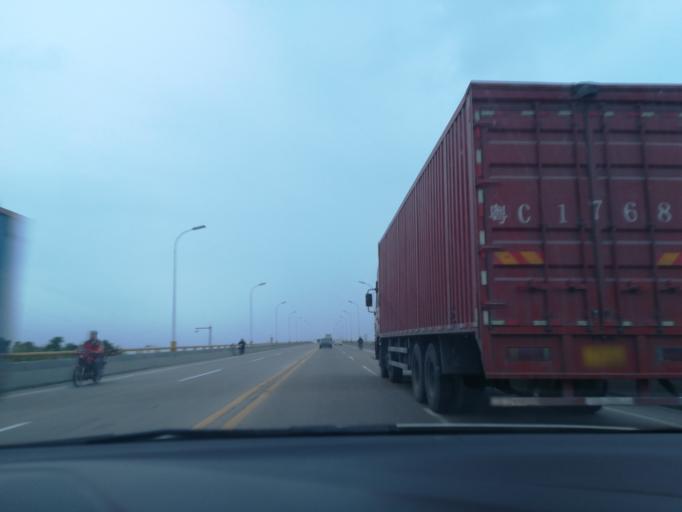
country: CN
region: Guangdong
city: Huangge
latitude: 22.7963
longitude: 113.4900
